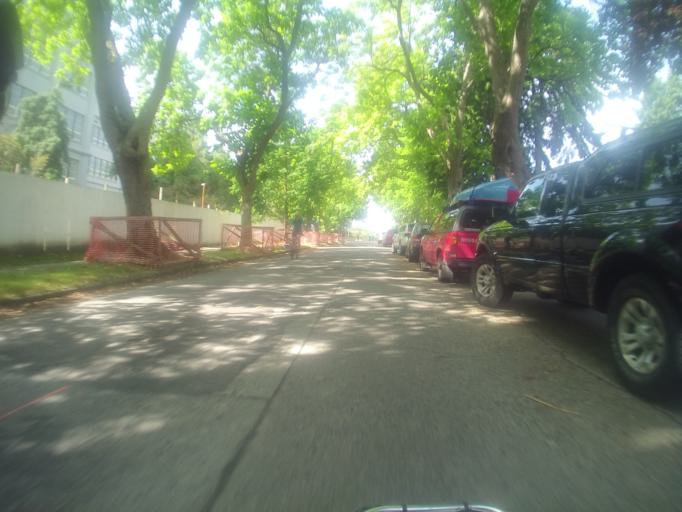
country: CA
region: British Columbia
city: West End
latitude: 49.2630
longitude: -123.1635
